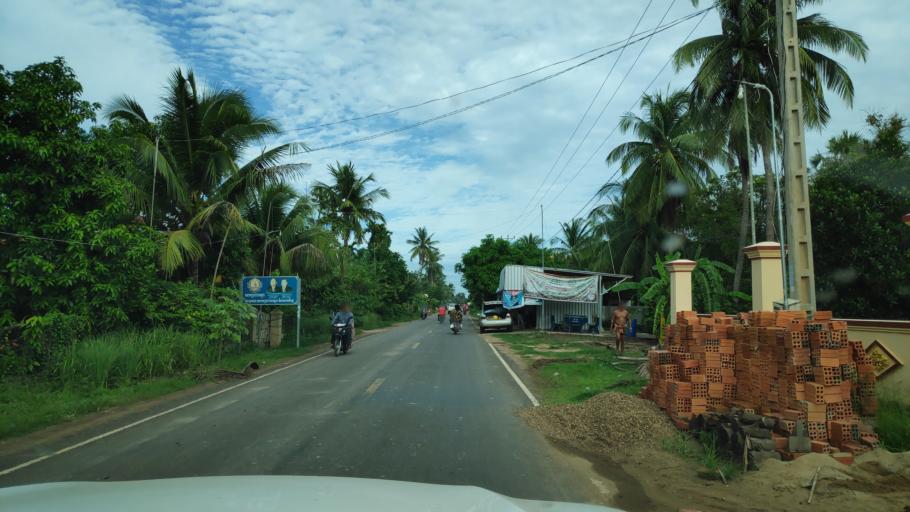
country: KH
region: Kampong Cham
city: Kampong Cham
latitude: 11.9465
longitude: 105.2533
